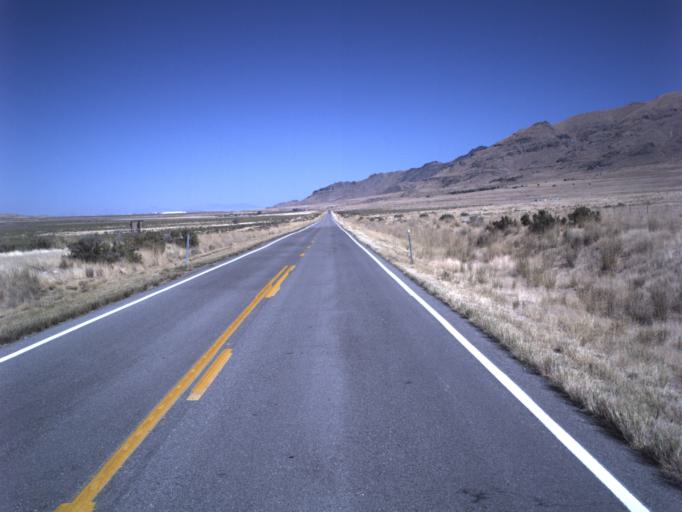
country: US
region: Utah
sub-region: Tooele County
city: Grantsville
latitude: 40.6455
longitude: -112.6872
